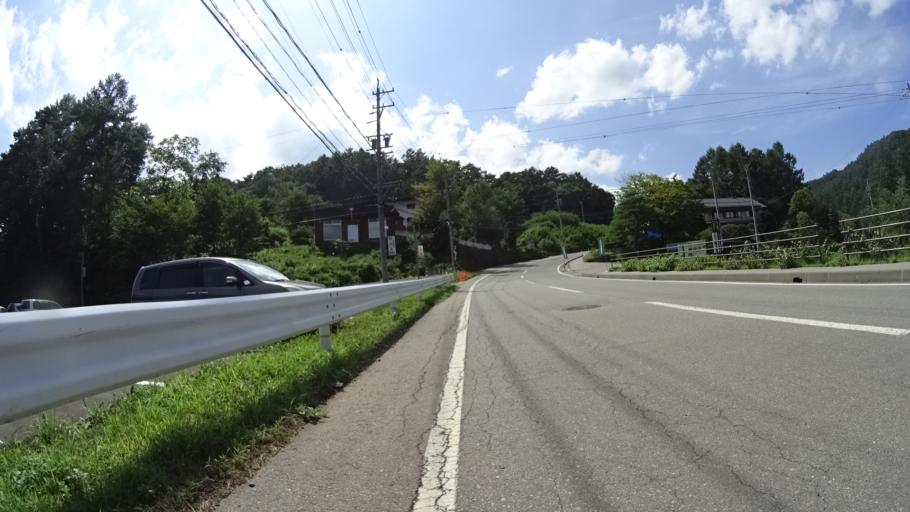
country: JP
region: Nagano
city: Saku
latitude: 36.0510
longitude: 138.4551
